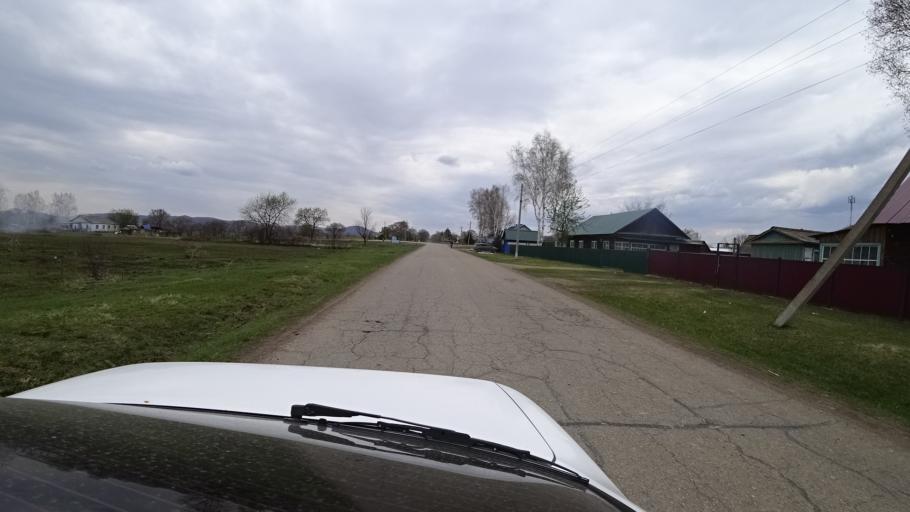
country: RU
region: Primorskiy
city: Novopokrovka
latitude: 45.5772
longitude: 134.3138
